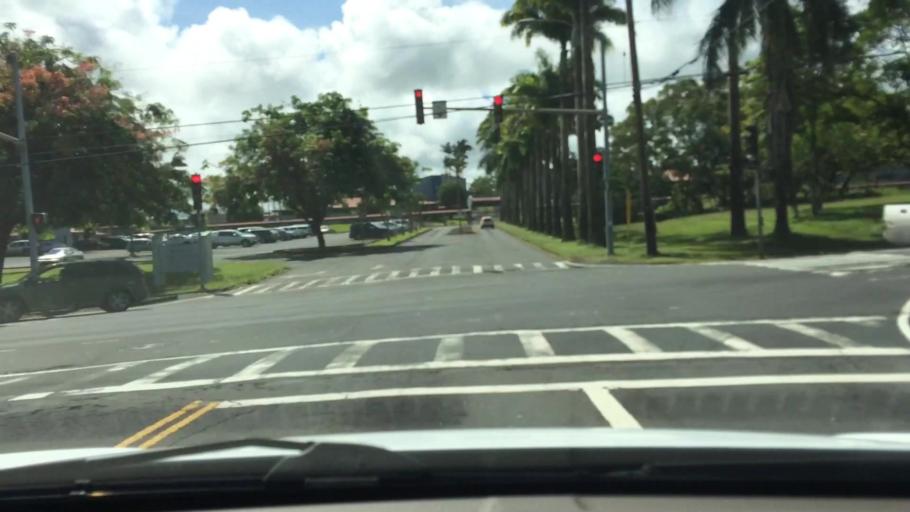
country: US
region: Hawaii
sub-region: Hawaii County
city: Hilo
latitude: 19.7011
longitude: -155.0774
